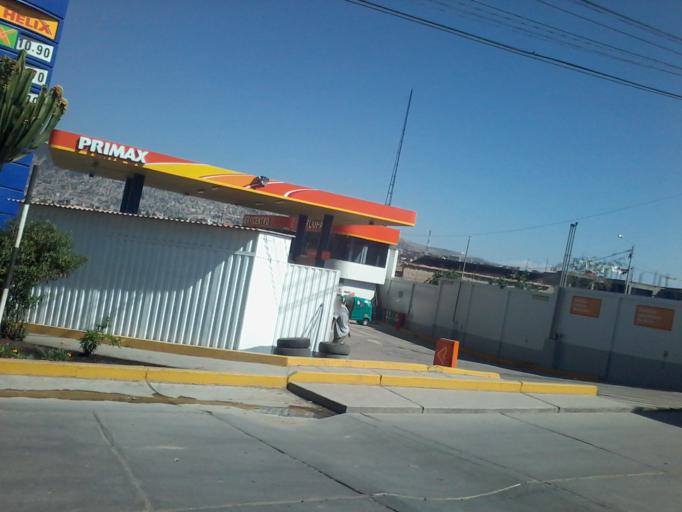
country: PE
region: Ayacucho
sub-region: Provincia de Huamanga
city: Ayacucho
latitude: -13.1577
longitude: -74.2075
